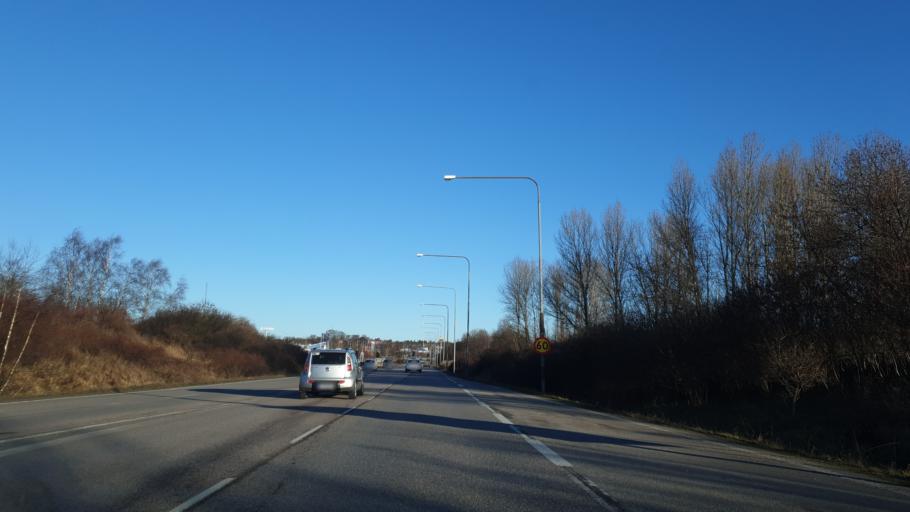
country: SE
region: Blekinge
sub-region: Karlskrona Kommun
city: Karlskrona
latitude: 56.1976
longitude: 15.6336
